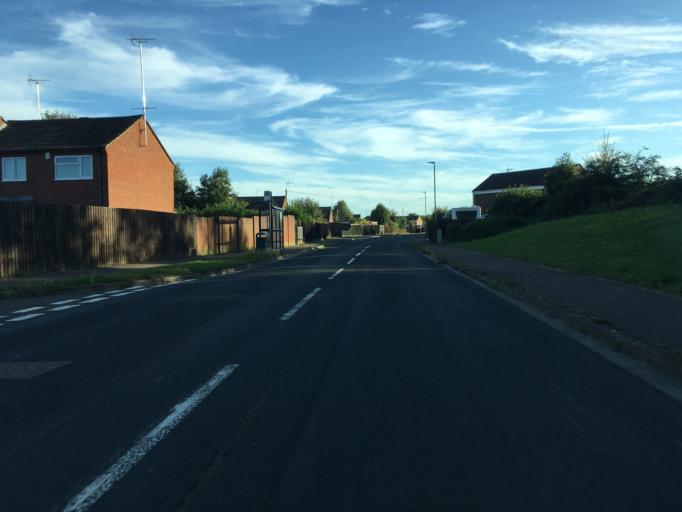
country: GB
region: England
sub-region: Worcestershire
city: Bredon
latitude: 52.0084
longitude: -2.1185
